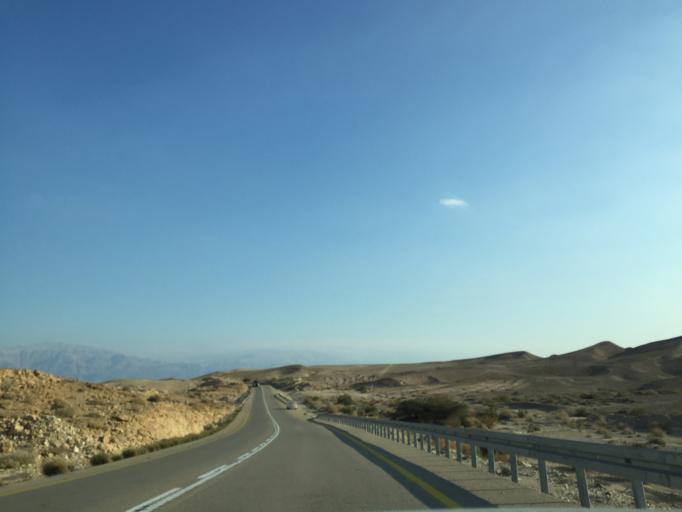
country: IL
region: Southern District
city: `En Boqeq
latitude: 31.1657
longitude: 35.3204
